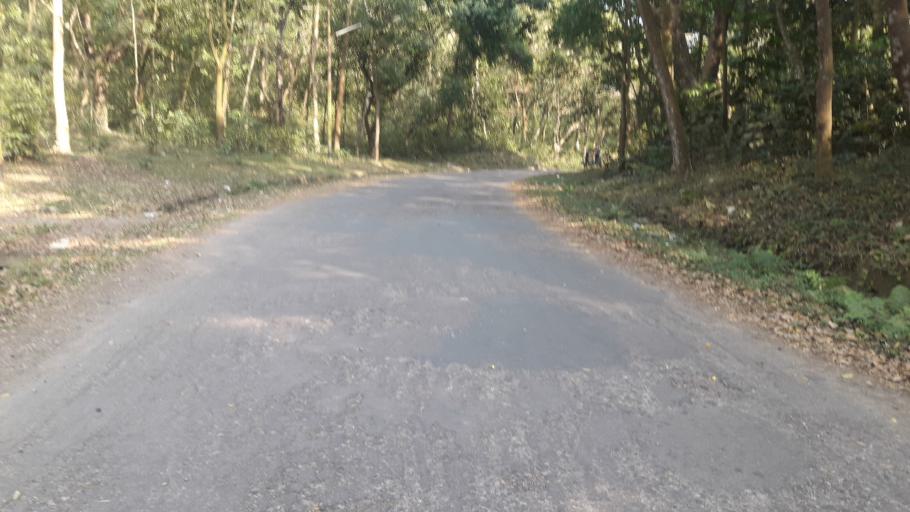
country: BD
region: Chittagong
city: Chittagong
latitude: 22.4670
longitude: 91.7891
